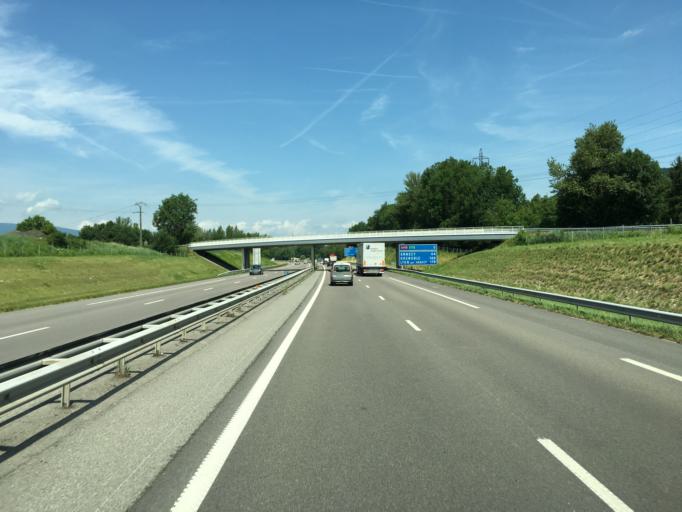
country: FR
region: Rhone-Alpes
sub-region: Departement de la Haute-Savoie
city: Bonneville
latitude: 46.0791
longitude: 6.3764
